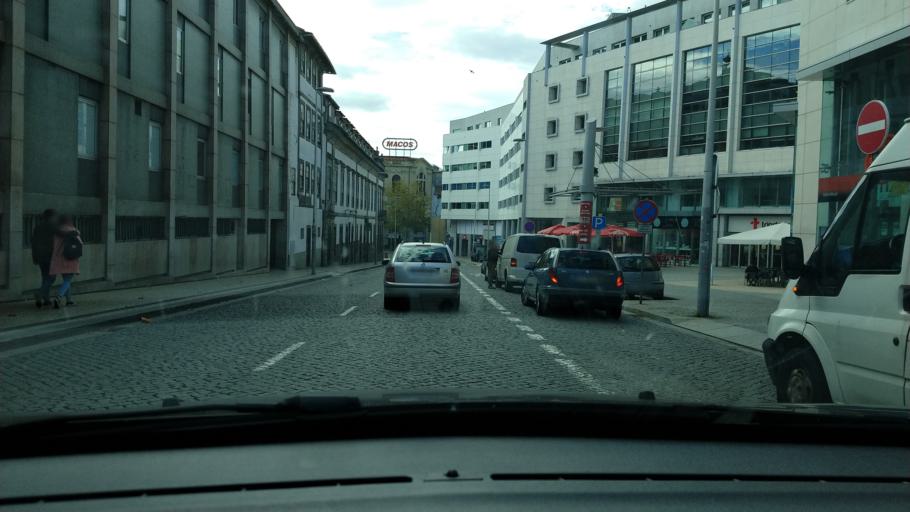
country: PT
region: Porto
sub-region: Porto
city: Porto
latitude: 41.1518
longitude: -8.6101
